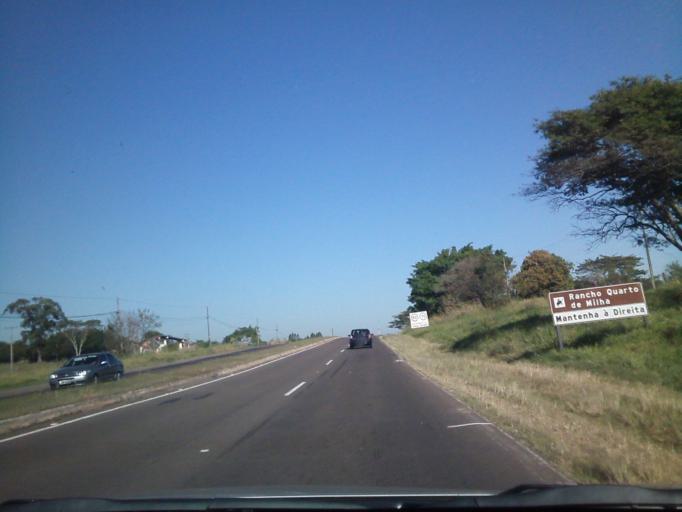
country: BR
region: Sao Paulo
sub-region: Presidente Prudente
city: Presidente Prudente
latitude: -22.1813
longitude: -51.4205
